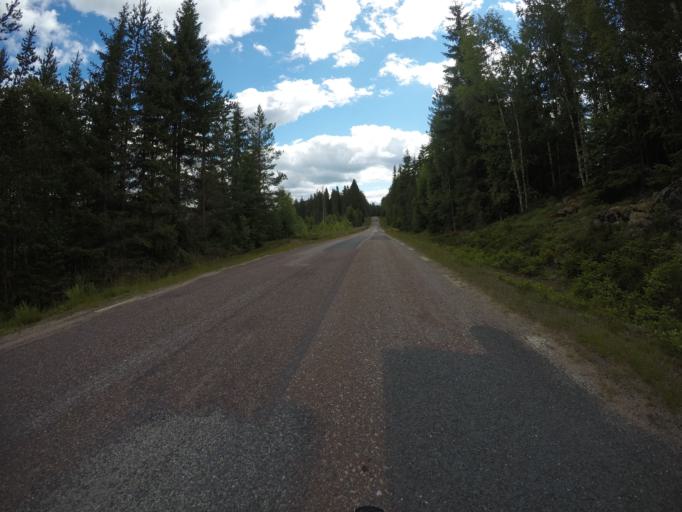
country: SE
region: OErebro
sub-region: Hallefors Kommun
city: Haellefors
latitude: 60.0729
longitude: 14.4905
